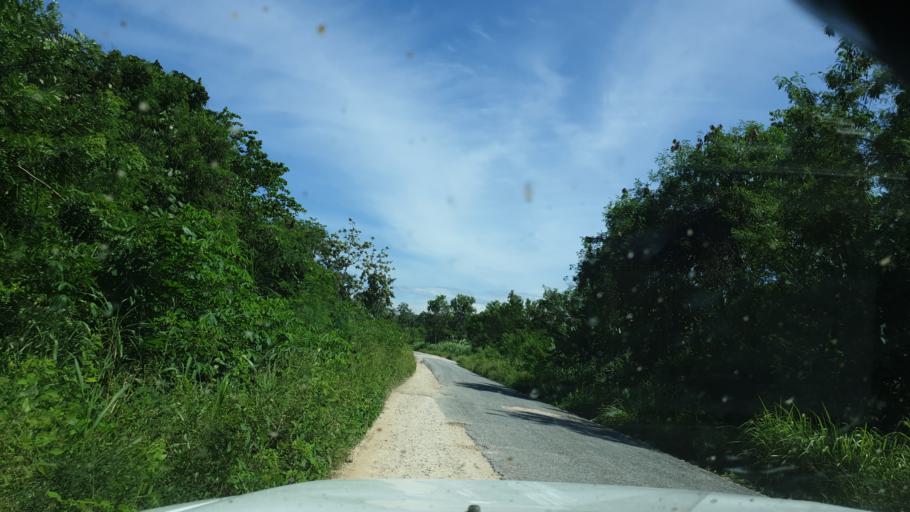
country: PG
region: Madang
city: Madang
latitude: -4.6807
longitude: 145.5954
